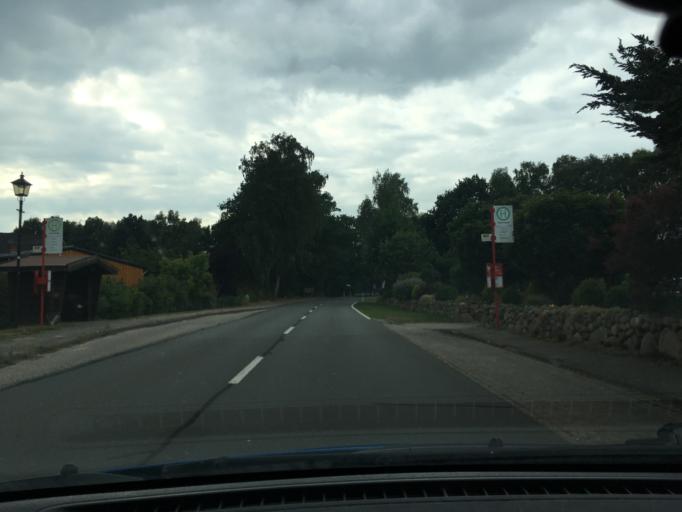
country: DE
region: Lower Saxony
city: Drestedt
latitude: 53.3350
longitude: 9.7576
